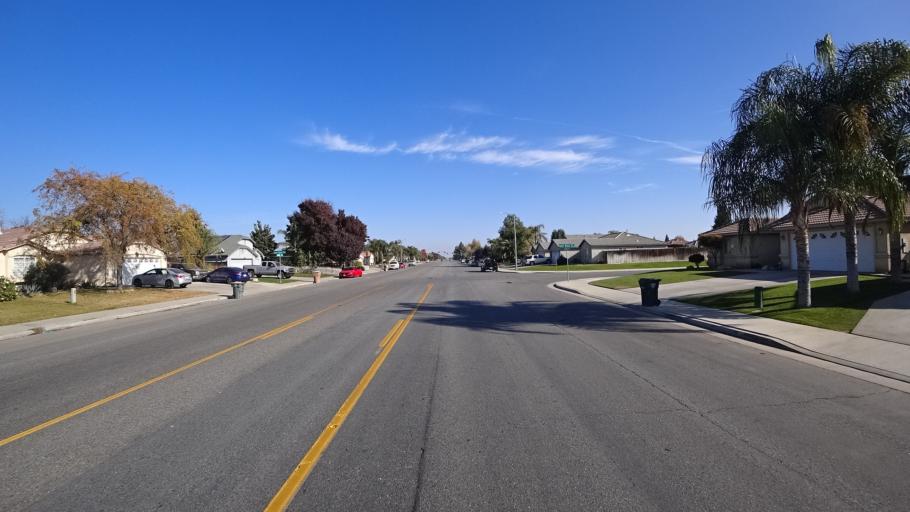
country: US
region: California
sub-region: Kern County
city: Greenfield
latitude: 35.2887
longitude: -119.0511
